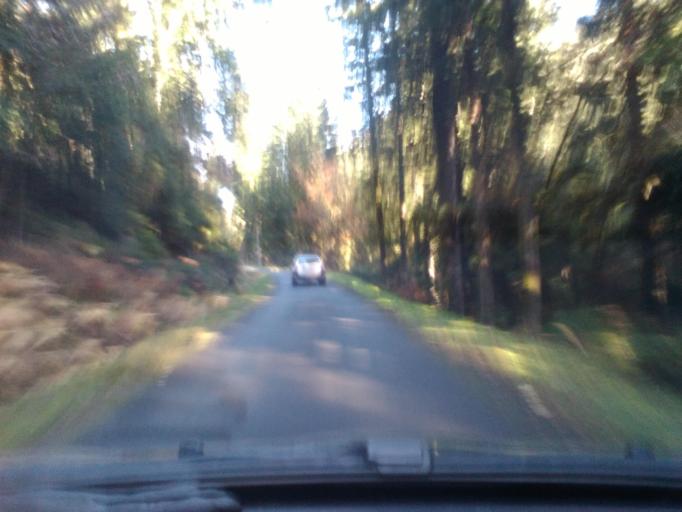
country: FR
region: Lorraine
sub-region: Departement des Vosges
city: Senones
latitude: 48.4575
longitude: 7.0586
